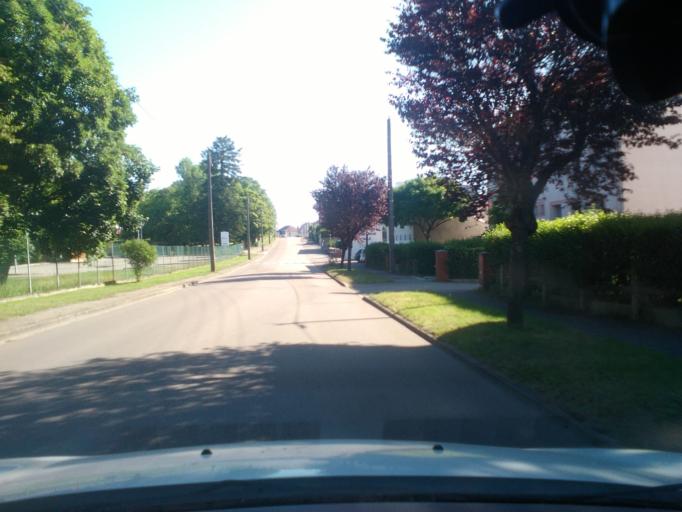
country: FR
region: Lorraine
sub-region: Departement des Vosges
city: Mirecourt
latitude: 48.2923
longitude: 6.1308
